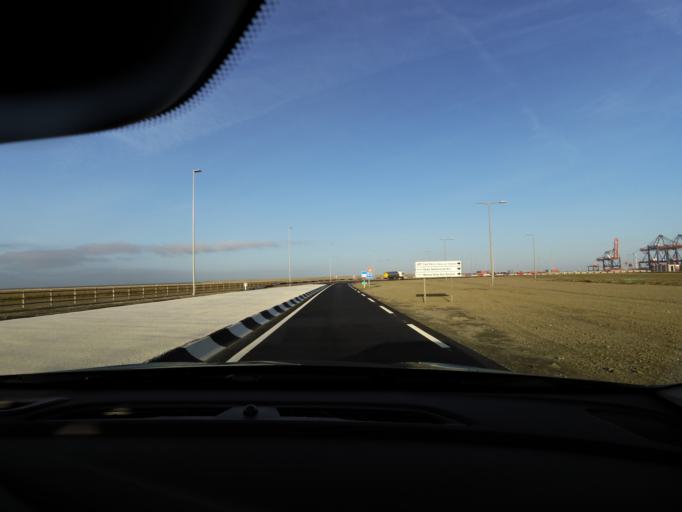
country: NL
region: South Holland
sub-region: Gemeente Rotterdam
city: Hoek van Holland
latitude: 51.9714
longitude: 4.0138
